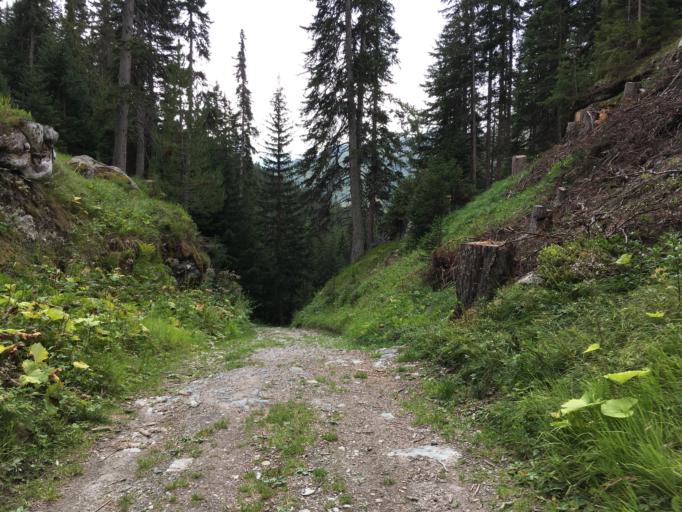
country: CH
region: Grisons
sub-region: Maloja District
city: Silvaplana
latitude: 46.4850
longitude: 9.6495
